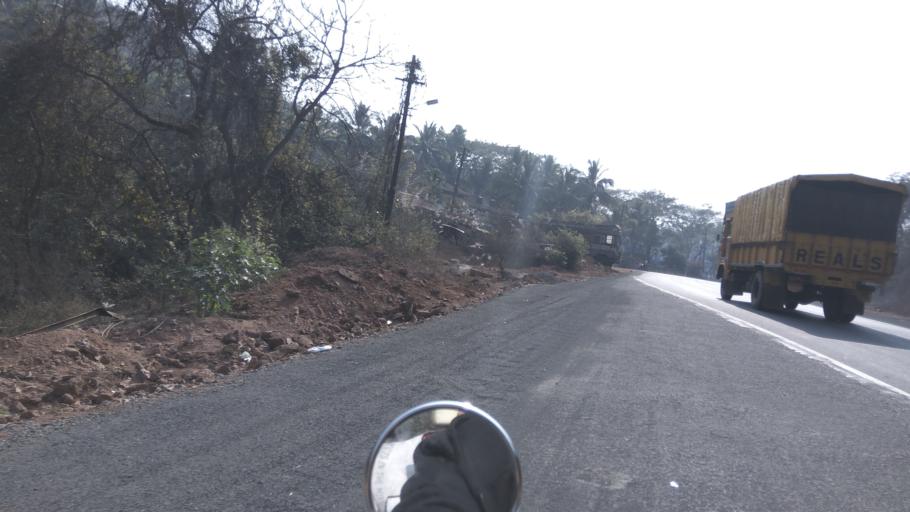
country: IN
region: Goa
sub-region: North Goa
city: Bandora
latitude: 15.4166
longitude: 73.9864
